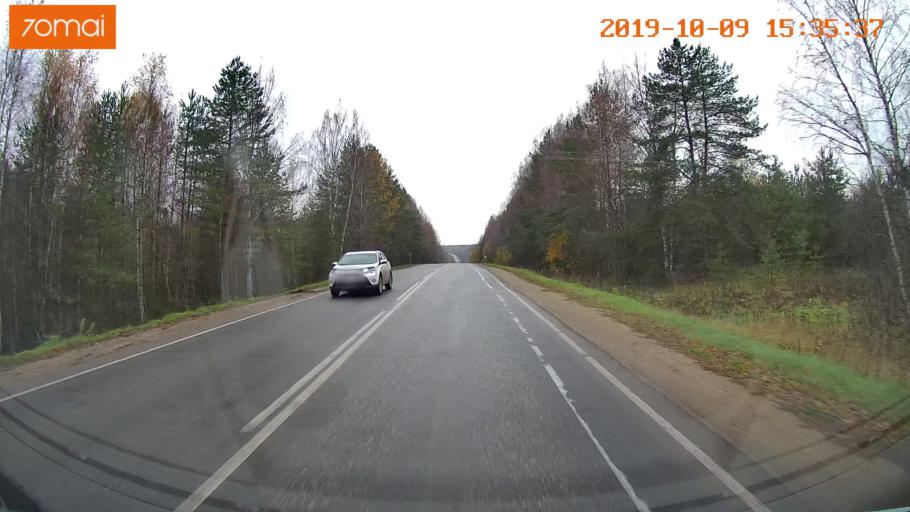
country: RU
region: Kostroma
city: Oktyabr'skiy
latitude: 57.9302
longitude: 41.2235
